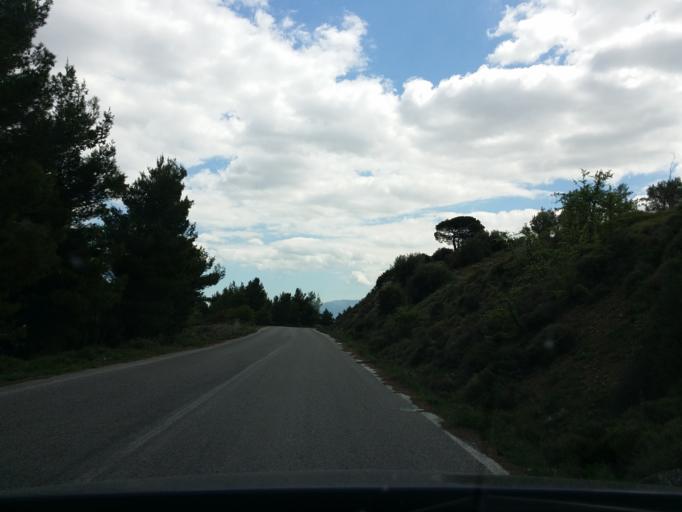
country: GR
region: Attica
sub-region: Nomarchia Dytikis Attikis
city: Fyli
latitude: 38.1208
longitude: 23.6501
